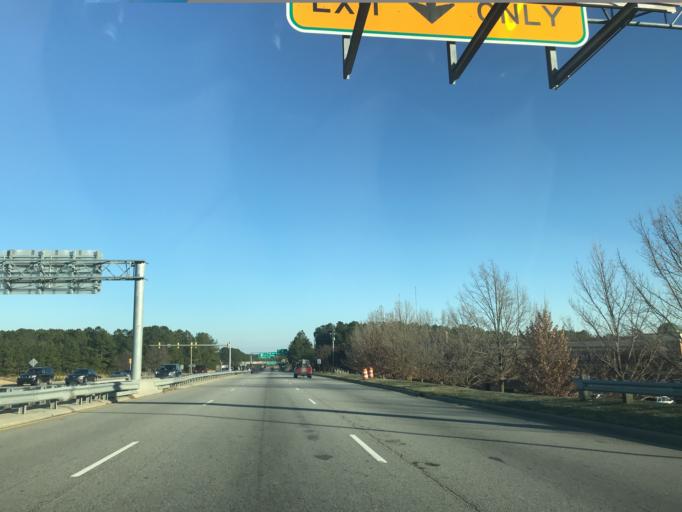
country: US
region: North Carolina
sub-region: Wake County
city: Garner
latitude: 35.6958
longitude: -78.5817
